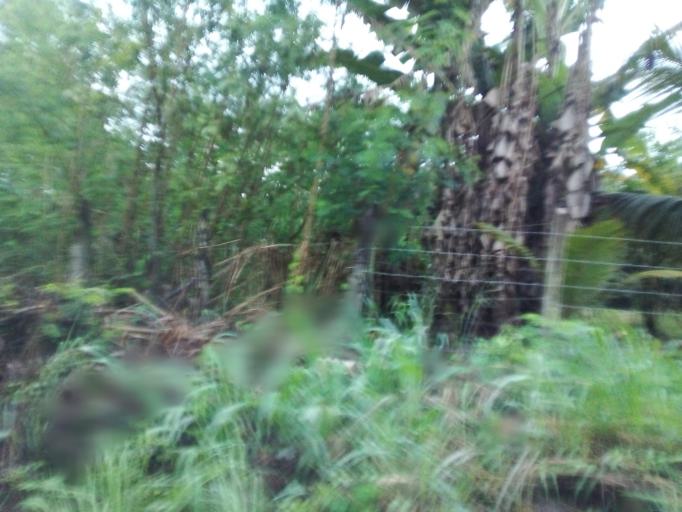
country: BR
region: Espirito Santo
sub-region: Marilandia
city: Marilandia
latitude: -19.5283
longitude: -40.4952
